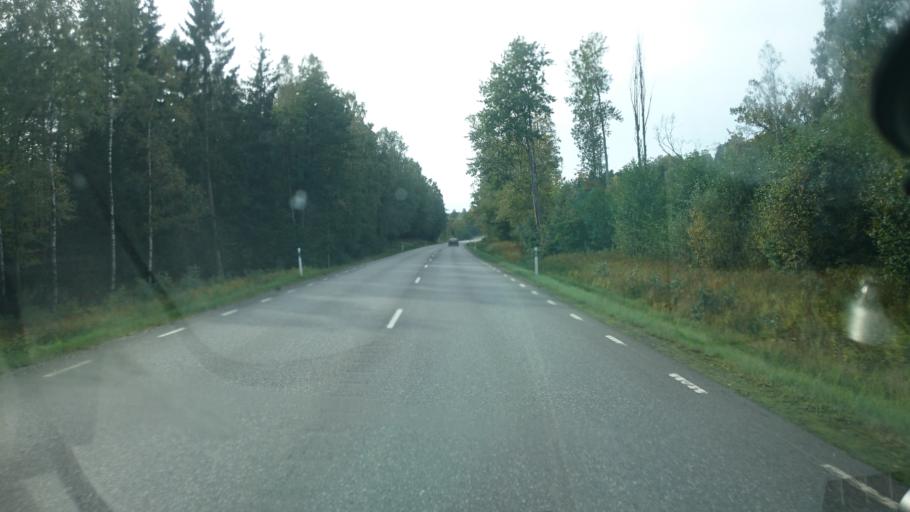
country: SE
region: Vaestra Goetaland
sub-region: Alingsas Kommun
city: Alingsas
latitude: 58.0173
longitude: 12.4534
